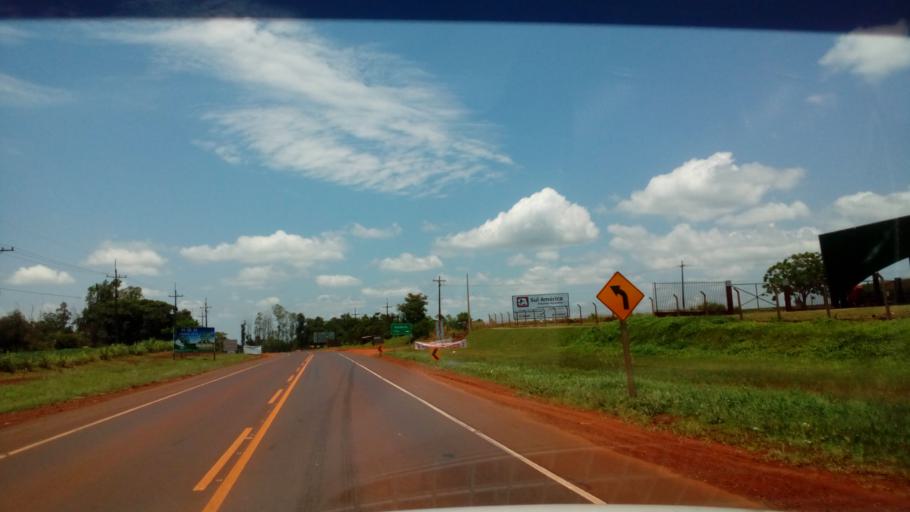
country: PY
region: Alto Parana
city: Naranjal
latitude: -25.9947
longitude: -55.1224
